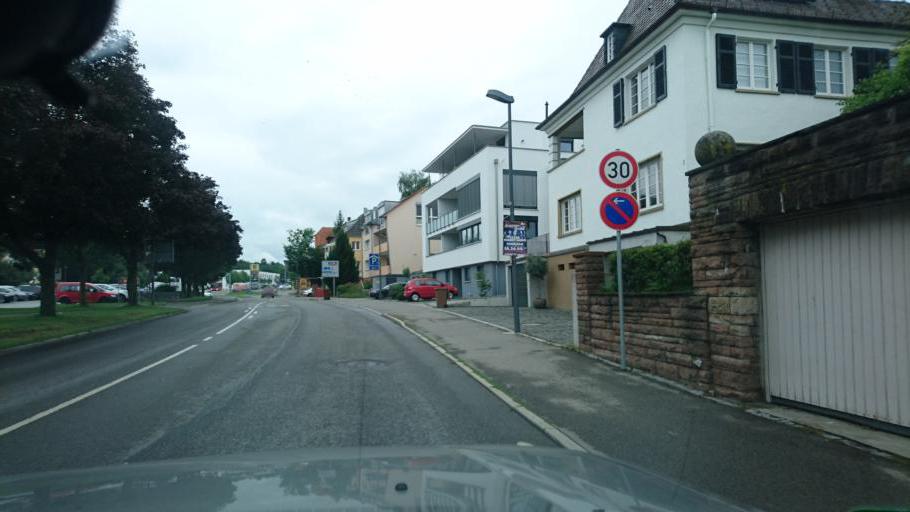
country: DE
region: Baden-Wuerttemberg
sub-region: Freiburg Region
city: Rottweil
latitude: 48.1702
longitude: 8.6248
